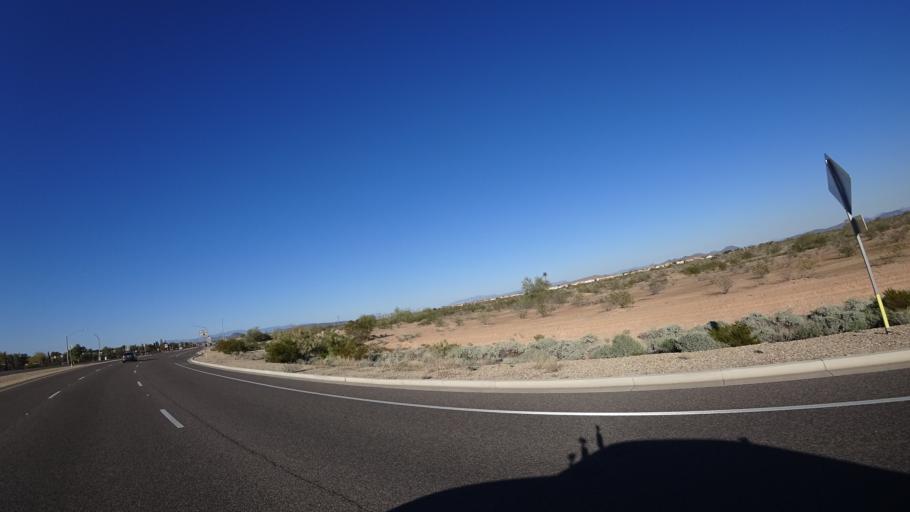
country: US
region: Arizona
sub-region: Maricopa County
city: Sun City West
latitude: 33.6878
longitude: -112.3336
